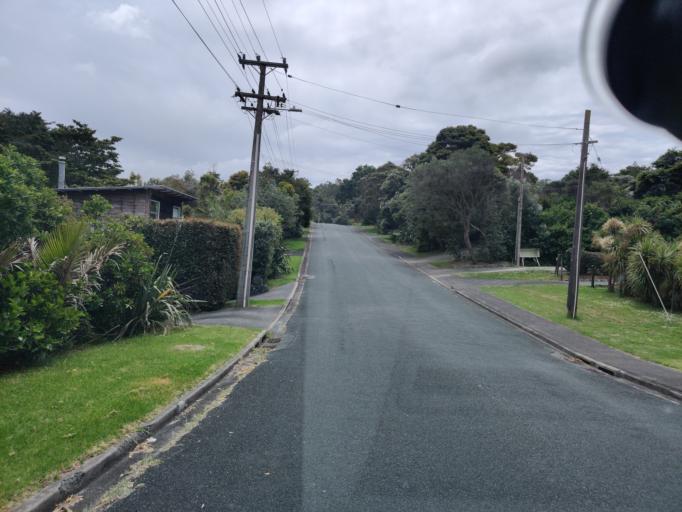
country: NZ
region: Auckland
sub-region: Auckland
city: Warkworth
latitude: -36.2974
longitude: 174.7980
